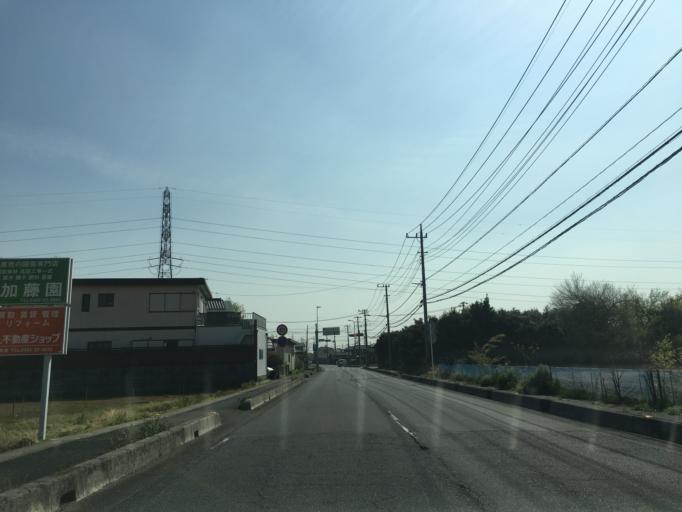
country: JP
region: Saitama
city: Sugito
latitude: 36.0105
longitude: 139.7218
